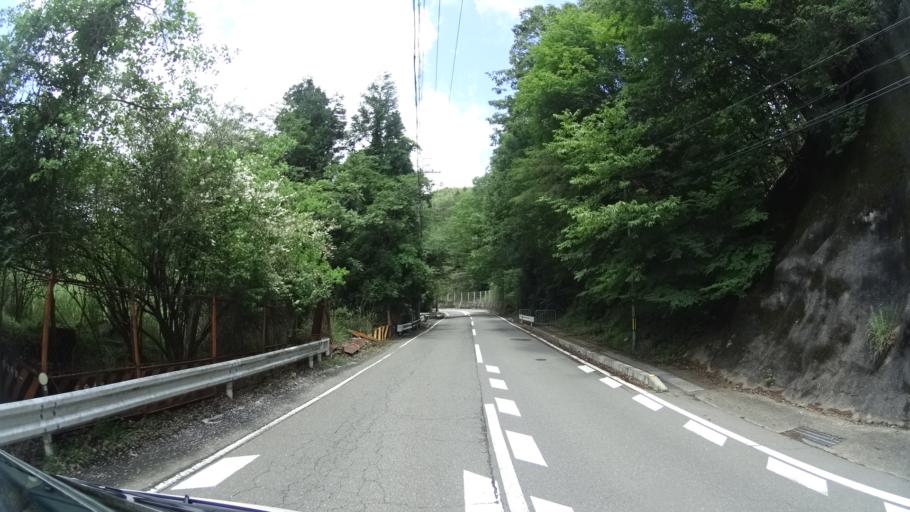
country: JP
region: Kyoto
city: Kameoka
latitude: 35.0208
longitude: 135.4037
